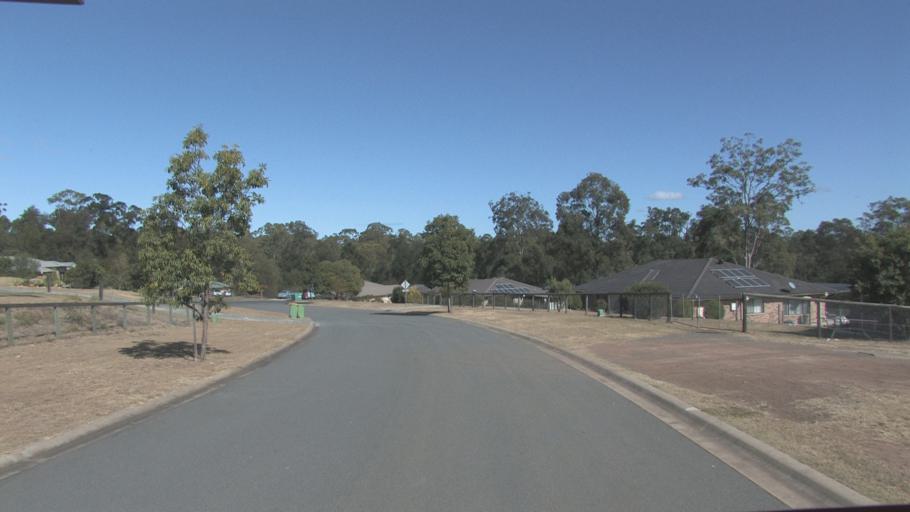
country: AU
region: Queensland
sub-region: Logan
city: Cedar Vale
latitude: -27.8910
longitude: 152.9984
